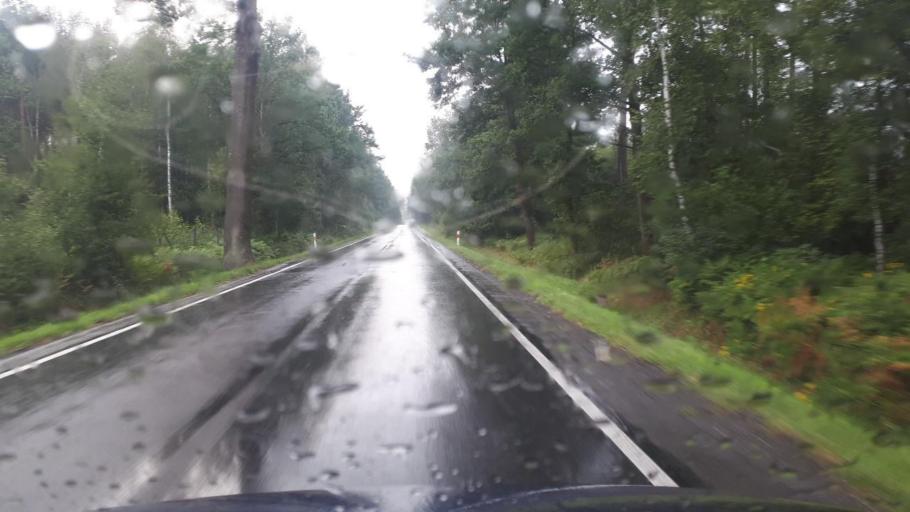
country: PL
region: Silesian Voivodeship
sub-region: Powiat tarnogorski
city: Tworog
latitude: 50.5295
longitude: 18.6712
